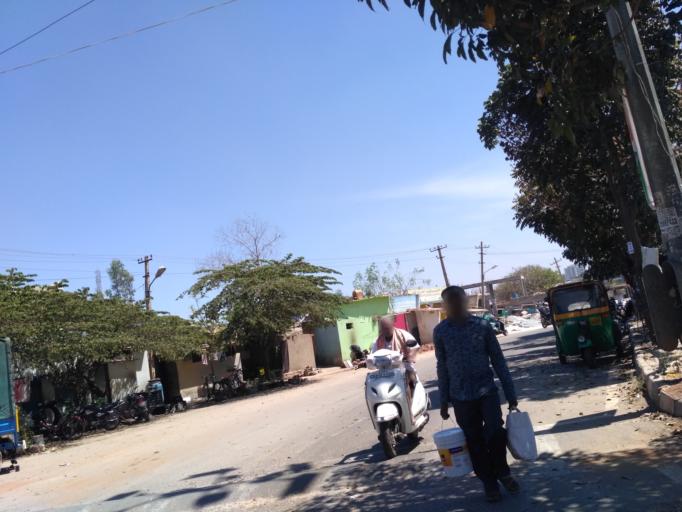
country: IN
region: Karnataka
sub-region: Bangalore Urban
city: Yelahanka
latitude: 13.0930
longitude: 77.5910
